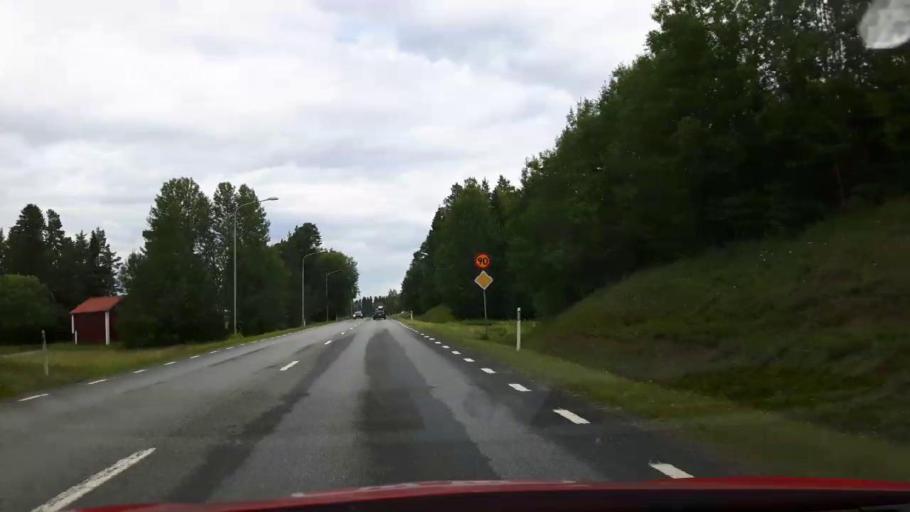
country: SE
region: Jaemtland
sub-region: Stroemsunds Kommun
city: Stroemsund
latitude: 63.6607
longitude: 15.3880
